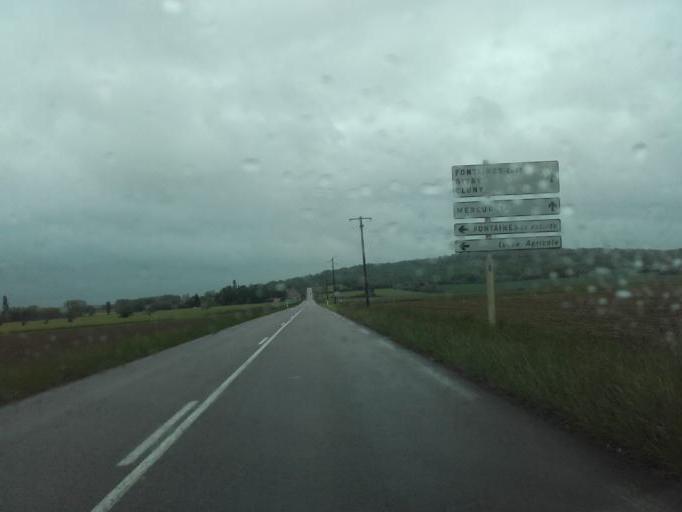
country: FR
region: Bourgogne
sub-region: Departement de Saone-et-Loire
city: Rully
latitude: 46.8666
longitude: 4.7525
